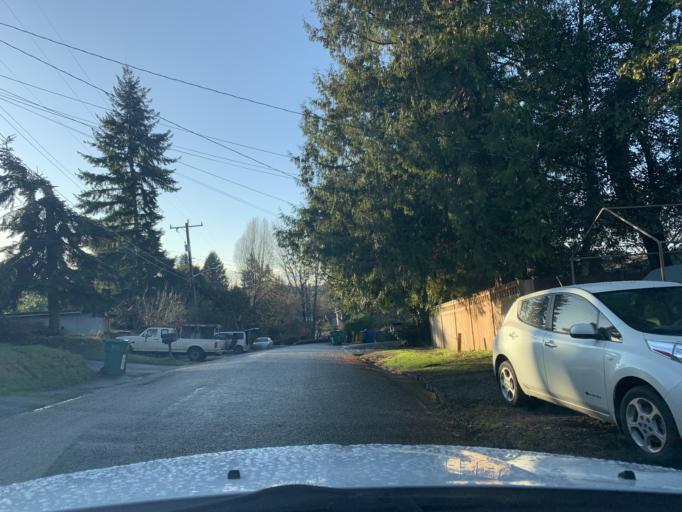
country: US
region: Washington
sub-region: King County
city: Shoreline
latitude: 47.6968
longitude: -122.3249
